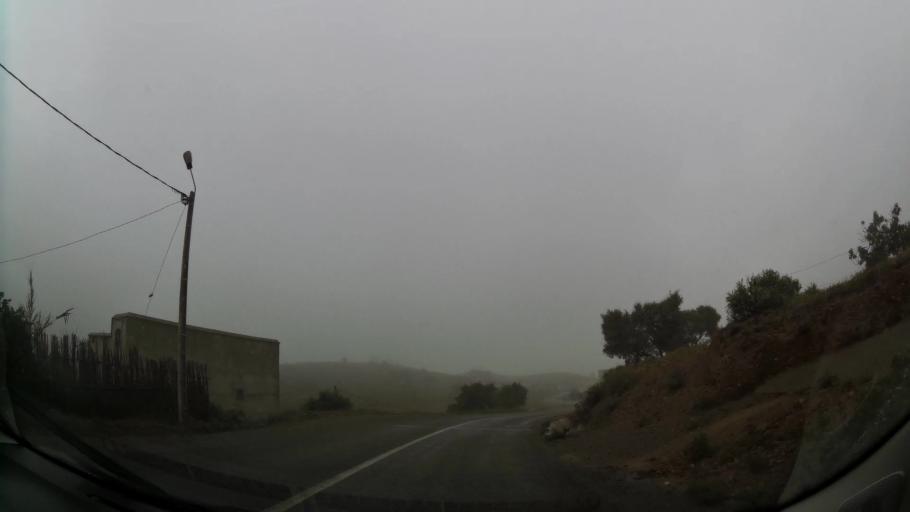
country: MA
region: Oriental
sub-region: Nador
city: Boudinar
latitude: 35.1269
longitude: -3.5799
